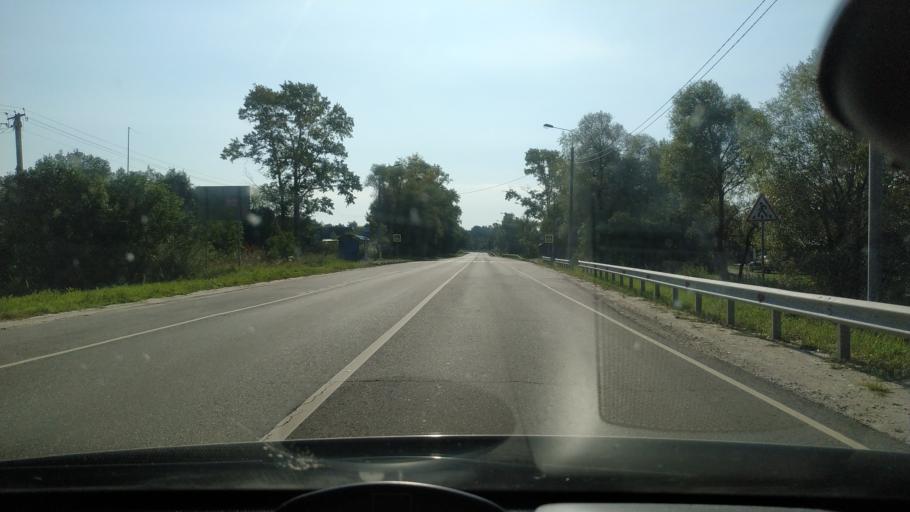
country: RU
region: Moskovskaya
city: Dmitrovskiy Pogost
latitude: 55.2341
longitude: 39.9076
